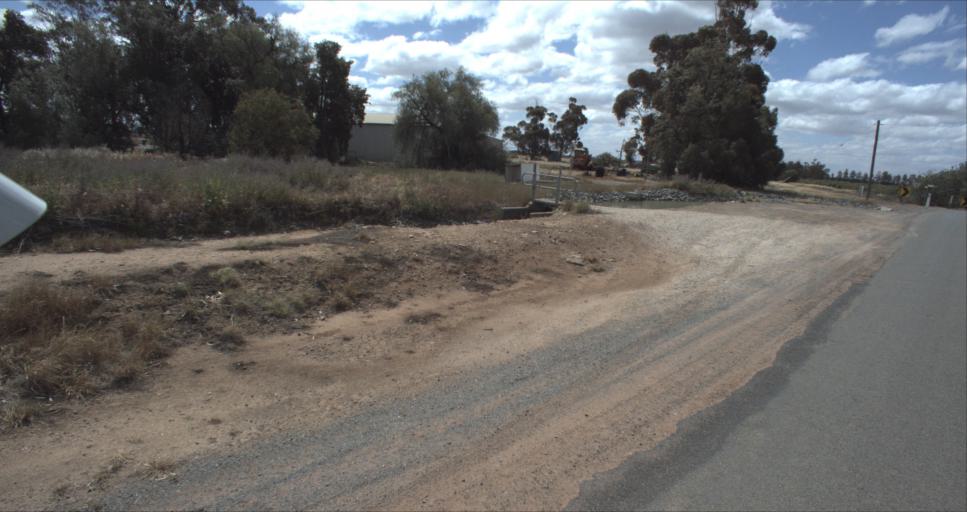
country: AU
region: New South Wales
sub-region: Leeton
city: Leeton
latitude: -34.5875
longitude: 146.3714
